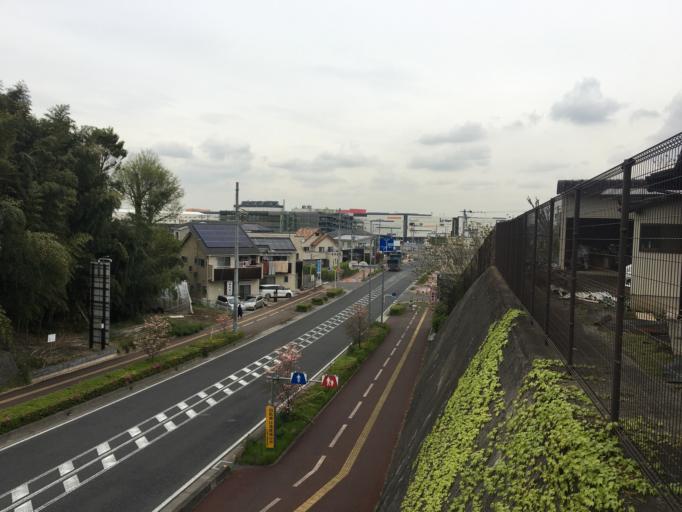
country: JP
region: Saitama
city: Oi
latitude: 35.8552
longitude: 139.5467
